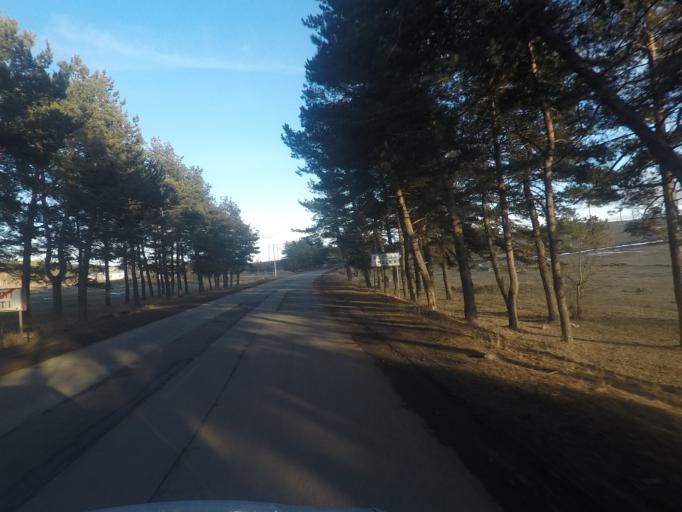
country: GE
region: Kvemo Kartli
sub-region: Tsalka
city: Tsalka
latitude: 41.6025
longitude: 44.0672
